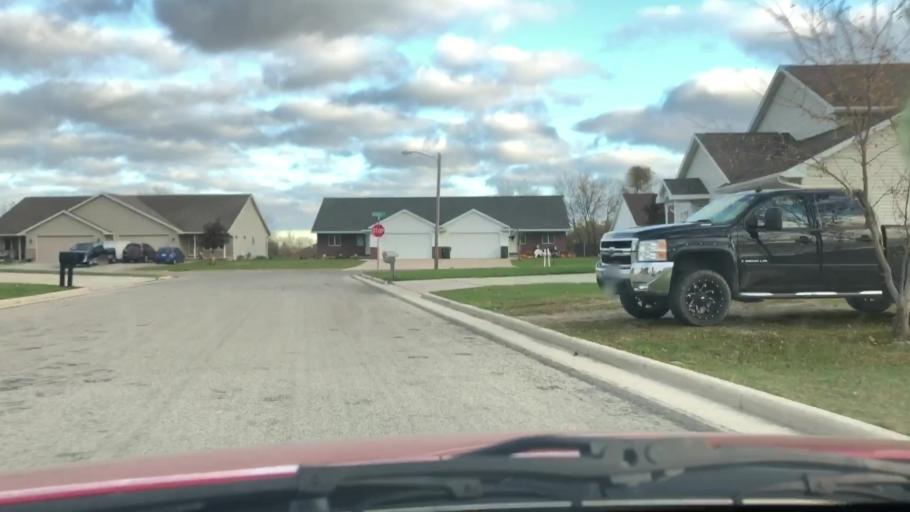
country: US
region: Wisconsin
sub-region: Outagamie County
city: Seymour
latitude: 44.5093
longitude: -88.3145
